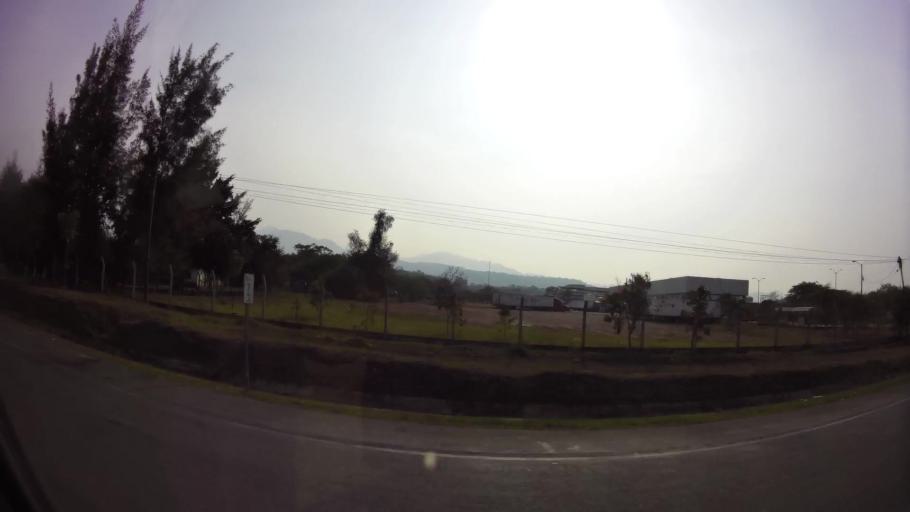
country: HN
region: La Paz
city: Yarumela
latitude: 14.3865
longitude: -87.6120
